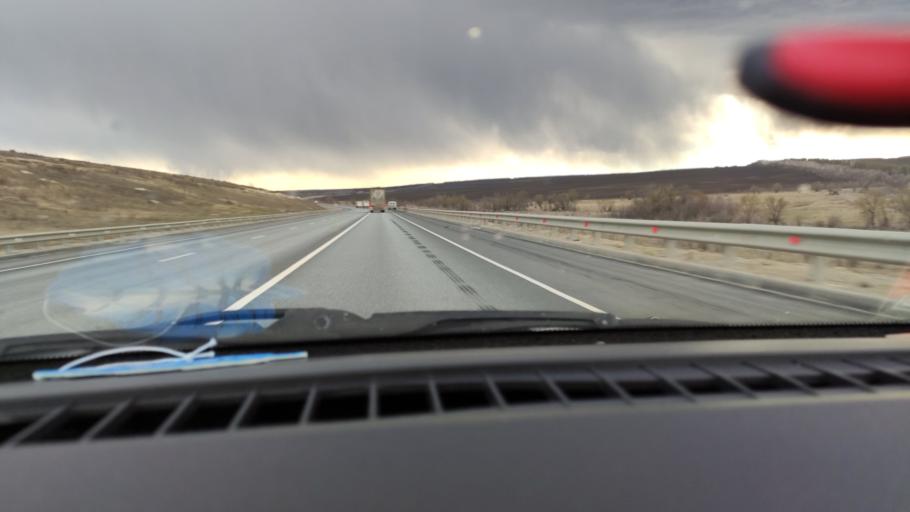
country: RU
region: Saratov
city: Yelshanka
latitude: 51.8712
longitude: 46.5045
